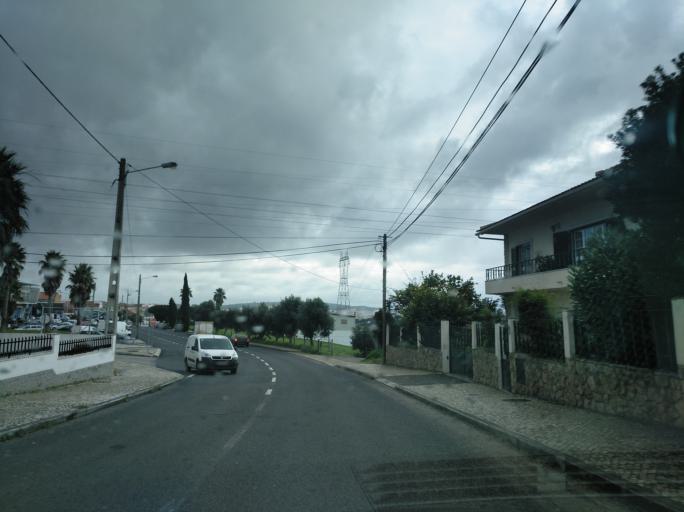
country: PT
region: Lisbon
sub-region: Odivelas
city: Famoes
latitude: 38.7872
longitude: -9.2093
